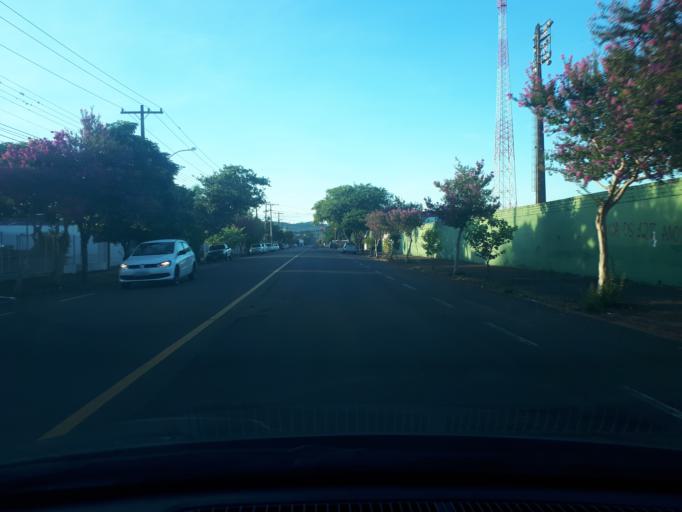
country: BR
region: Rio Grande do Sul
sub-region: Santa Cruz Do Sul
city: Santa Cruz do Sul
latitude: -29.7065
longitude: -52.4415
